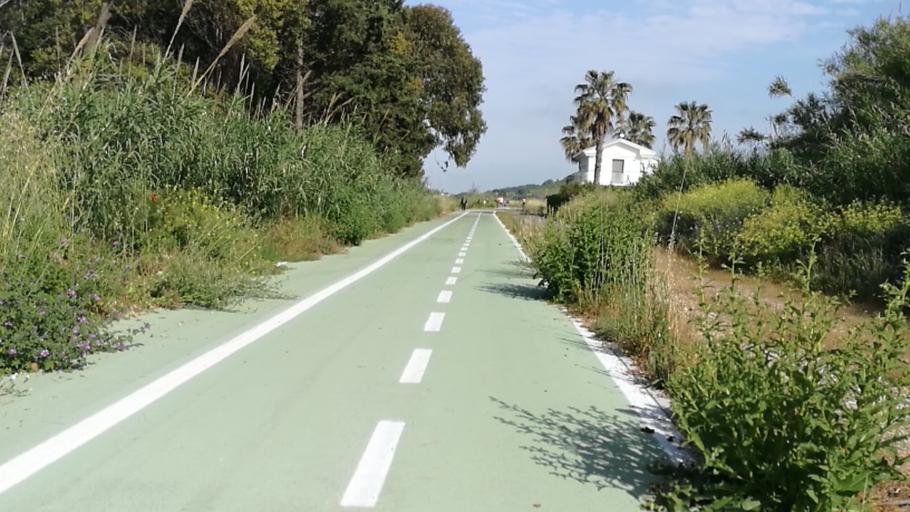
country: IT
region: Abruzzo
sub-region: Provincia di Chieti
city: Casalbordino-Miracoli
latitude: 42.2051
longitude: 14.6025
